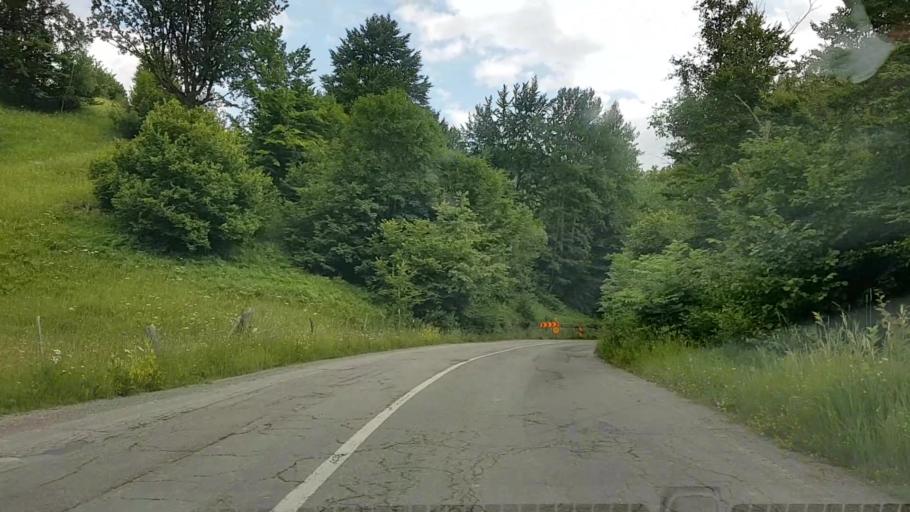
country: RO
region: Neamt
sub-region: Comuna Pangarati
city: Pangarati
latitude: 46.9393
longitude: 26.1274
